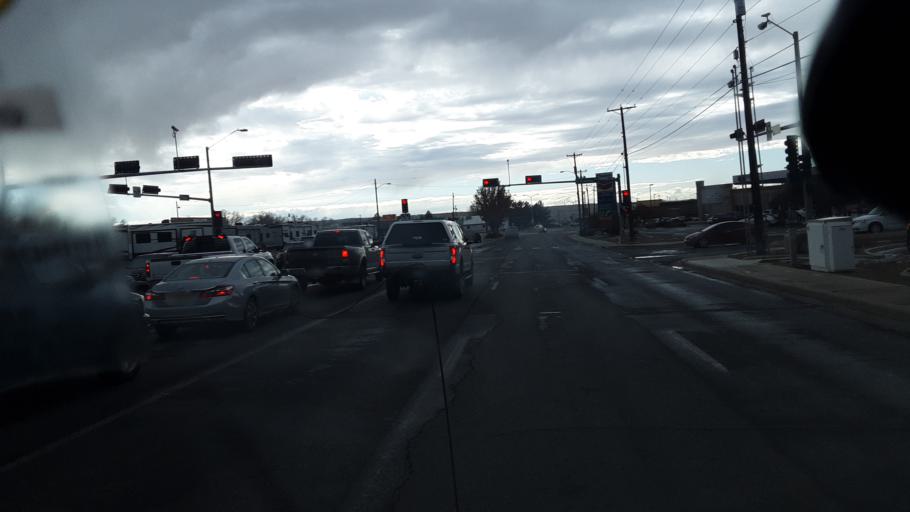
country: US
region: New Mexico
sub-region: San Juan County
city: Farmington
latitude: 36.7432
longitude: -108.1676
